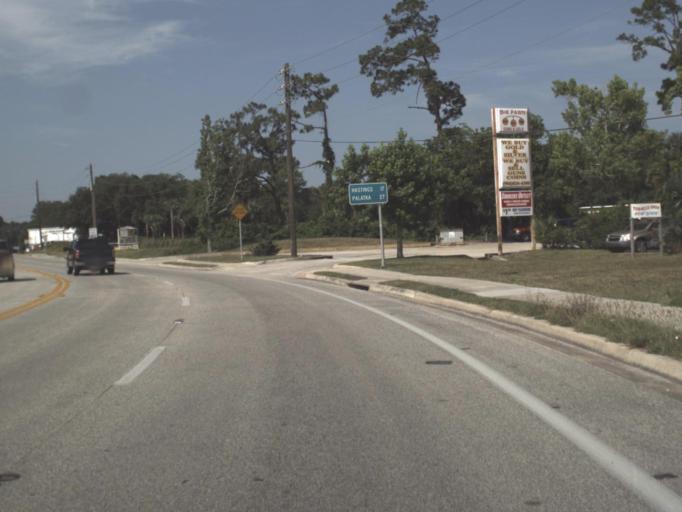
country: US
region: Florida
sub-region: Saint Johns County
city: Saint Augustine
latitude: 29.8804
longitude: -81.3272
